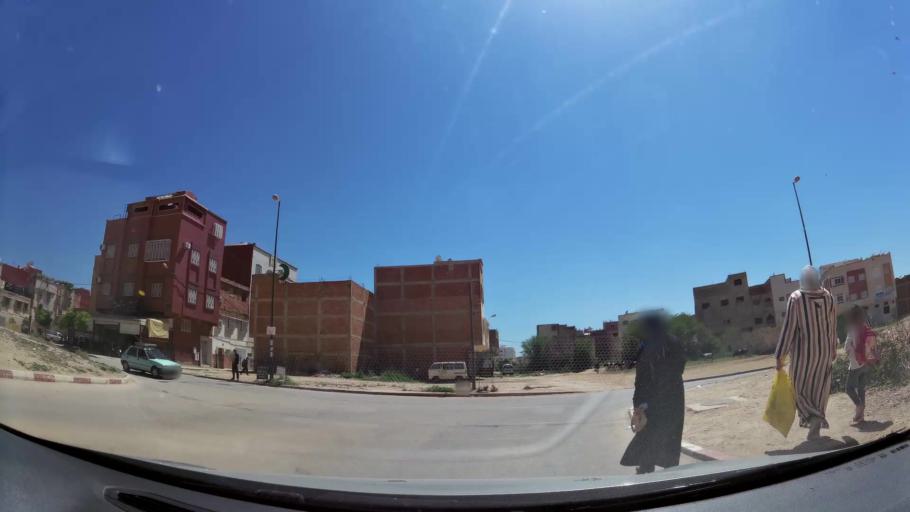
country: MA
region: Meknes-Tafilalet
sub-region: Meknes
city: Meknes
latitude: 33.8680
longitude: -5.5611
